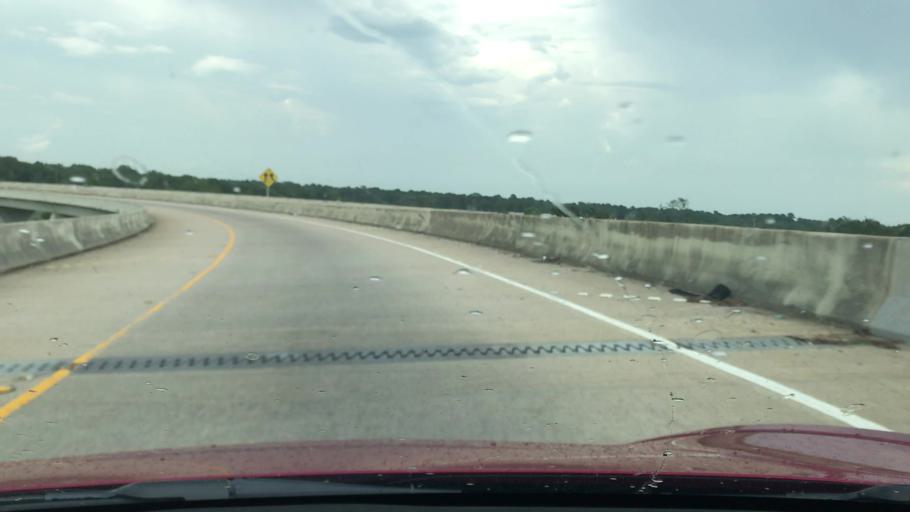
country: US
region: Louisiana
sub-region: Bossier Parish
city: Bossier City
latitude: 32.4198
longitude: -93.7489
